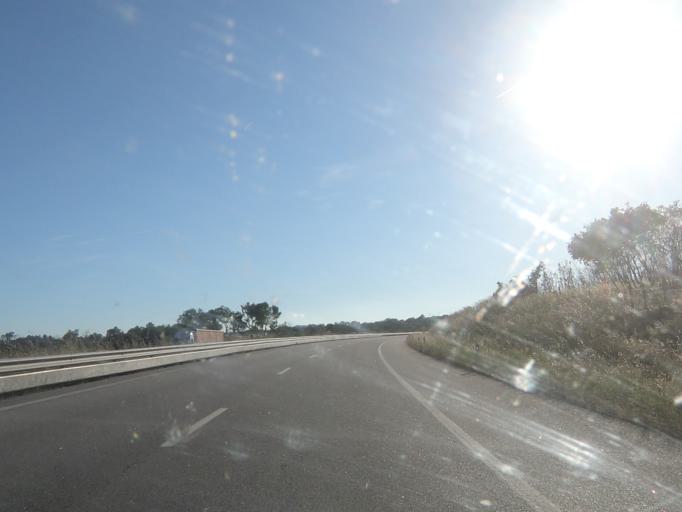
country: PT
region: Guarda
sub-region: Pinhel
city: Pinhel
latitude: 40.6035
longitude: -7.0460
